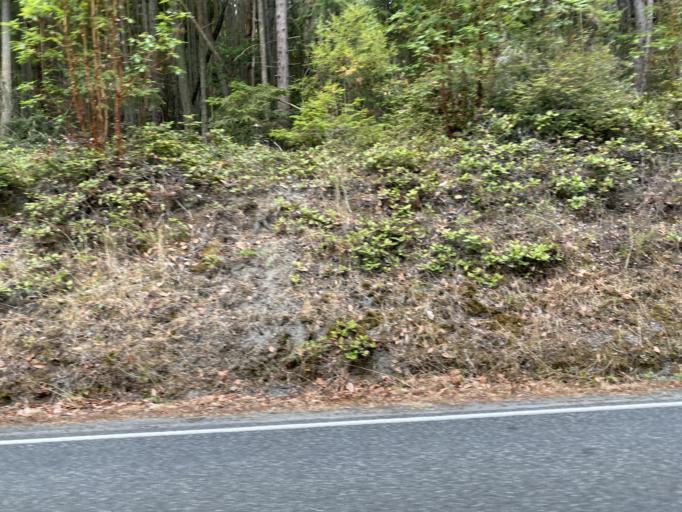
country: US
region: Washington
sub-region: Island County
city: Coupeville
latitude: 48.2146
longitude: -122.7242
